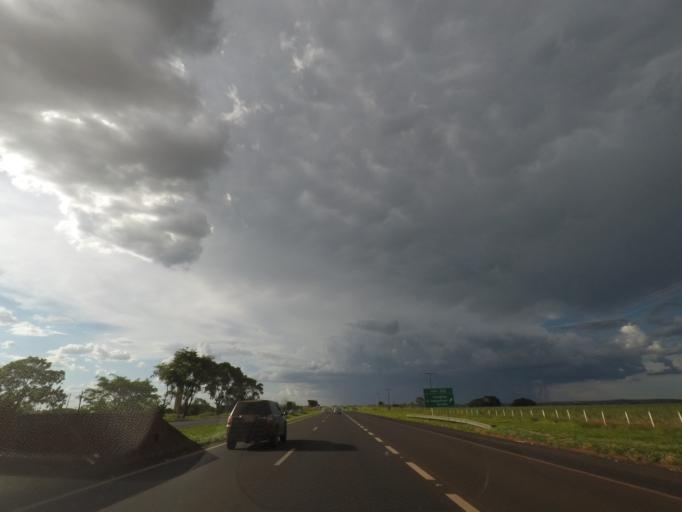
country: BR
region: Sao Paulo
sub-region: Jardinopolis
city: Jardinopolis
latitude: -21.0868
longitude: -47.7987
